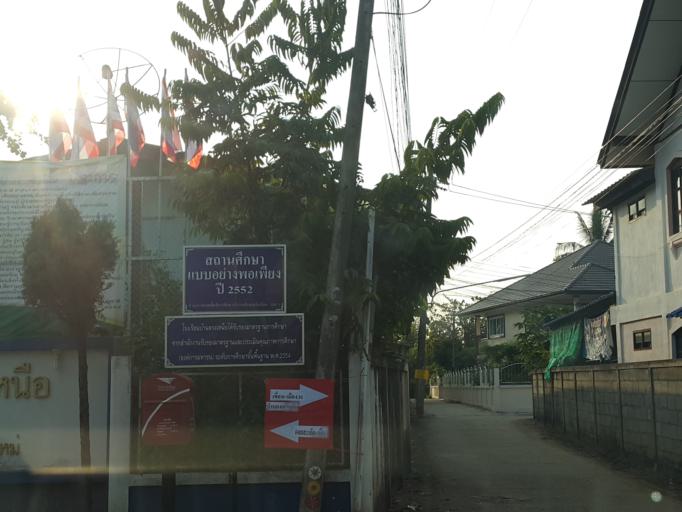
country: TH
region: Chiang Mai
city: San Sai
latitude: 18.8788
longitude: 99.1238
